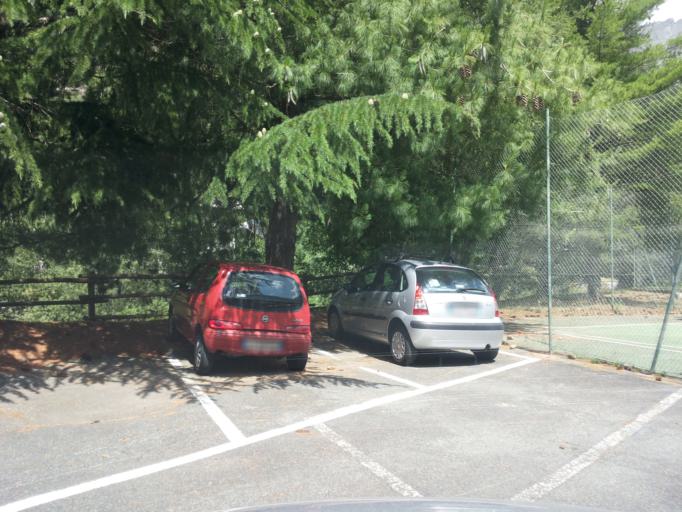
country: IT
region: Aosta Valley
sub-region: Valle d'Aosta
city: Gaby
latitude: 45.7034
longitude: 7.8776
